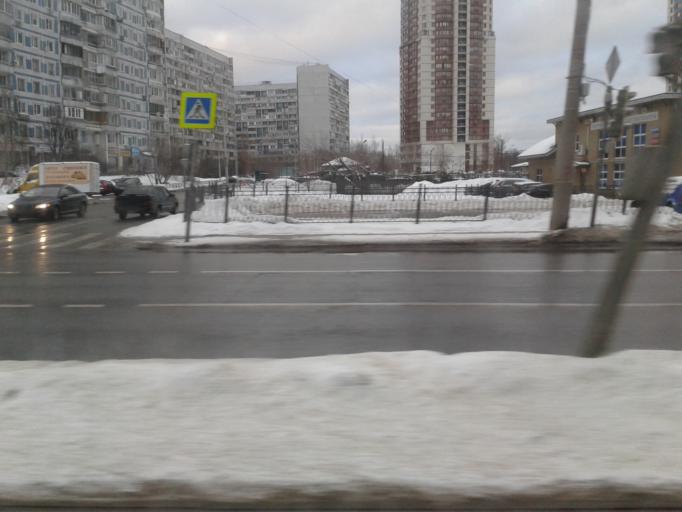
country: RU
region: Moscow
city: Strogino
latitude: 55.8041
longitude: 37.4218
